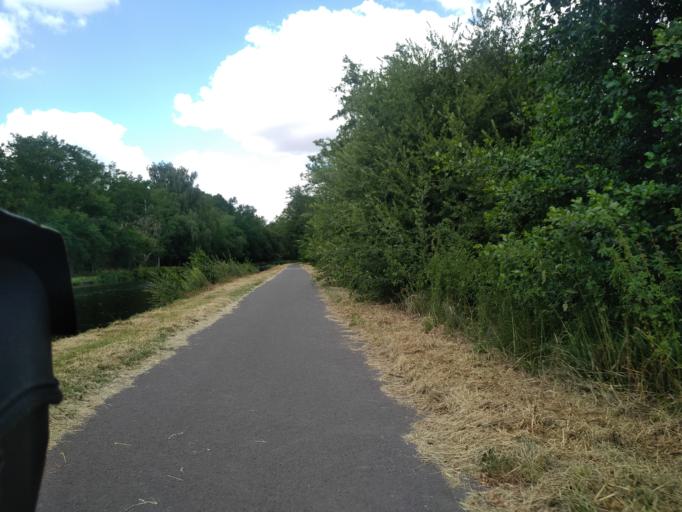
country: FR
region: Rhone-Alpes
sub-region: Departement de la Loire
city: Briennon
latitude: 46.1402
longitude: 4.0806
